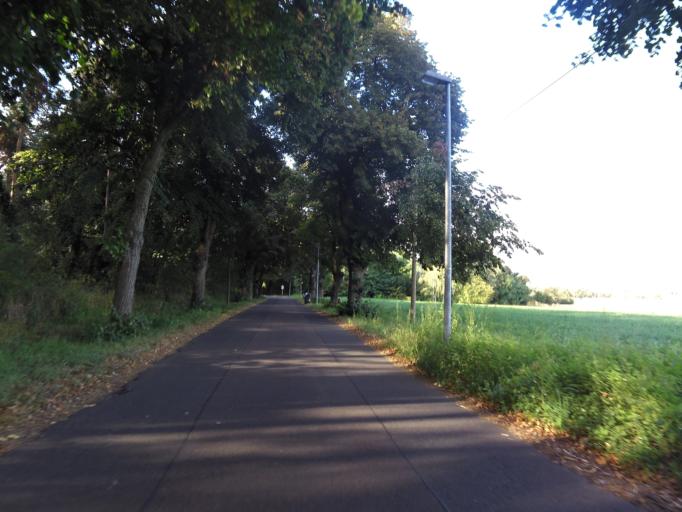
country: DE
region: Saxony
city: Schkeuditz
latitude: 51.3491
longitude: 12.2523
